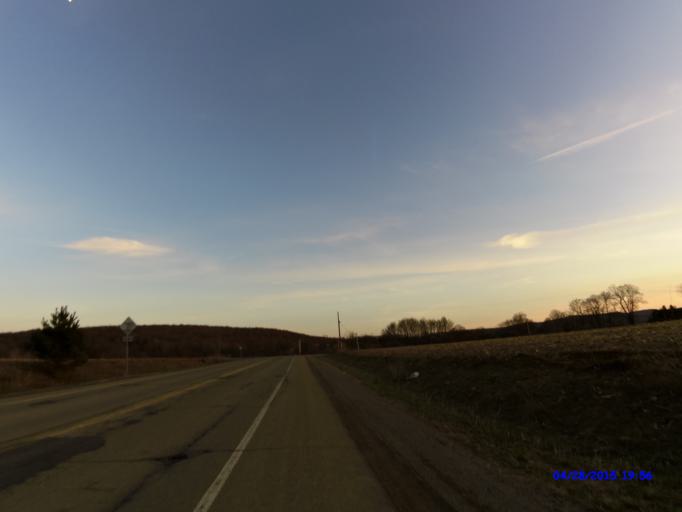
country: US
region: New York
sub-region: Cattaraugus County
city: Franklinville
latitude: 42.3750
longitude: -78.4446
